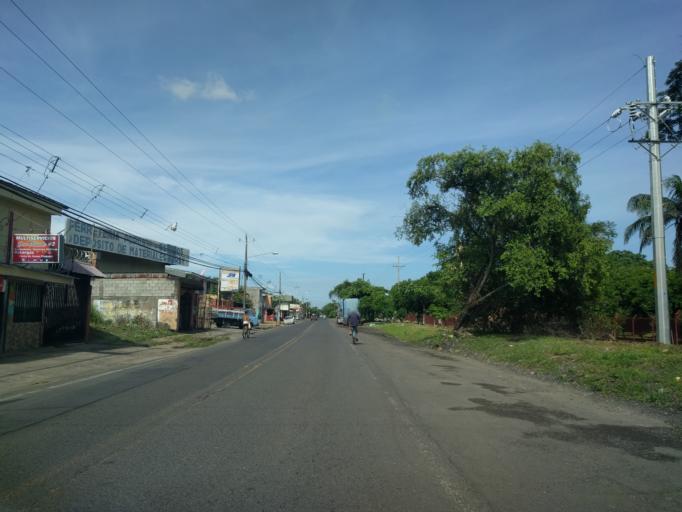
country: CR
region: Puntarenas
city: Esparza
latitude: 9.9892
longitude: -84.7132
